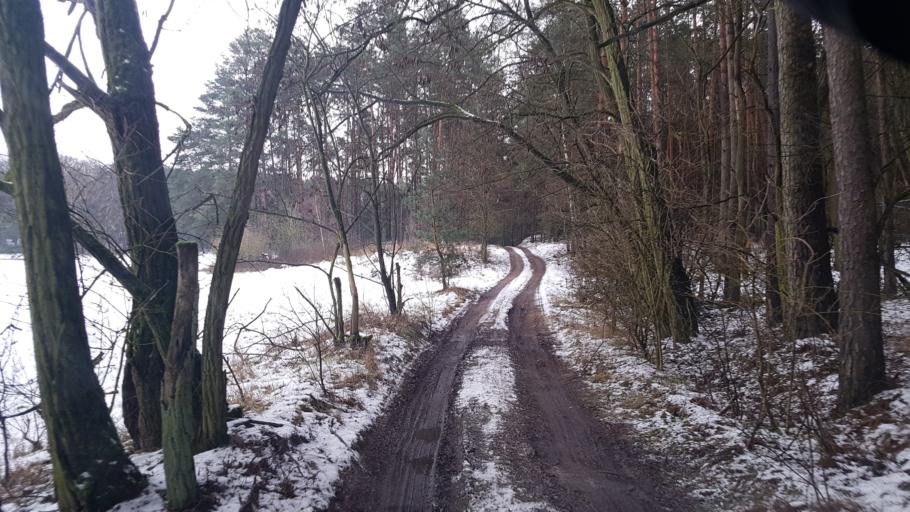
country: DE
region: Brandenburg
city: Schenkendobern
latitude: 51.8994
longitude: 14.5920
